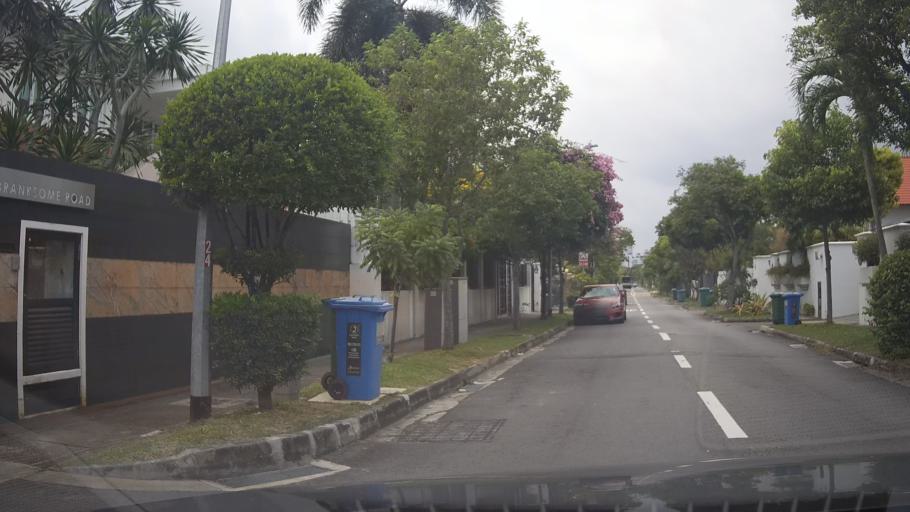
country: SG
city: Singapore
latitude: 1.3036
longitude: 103.8915
